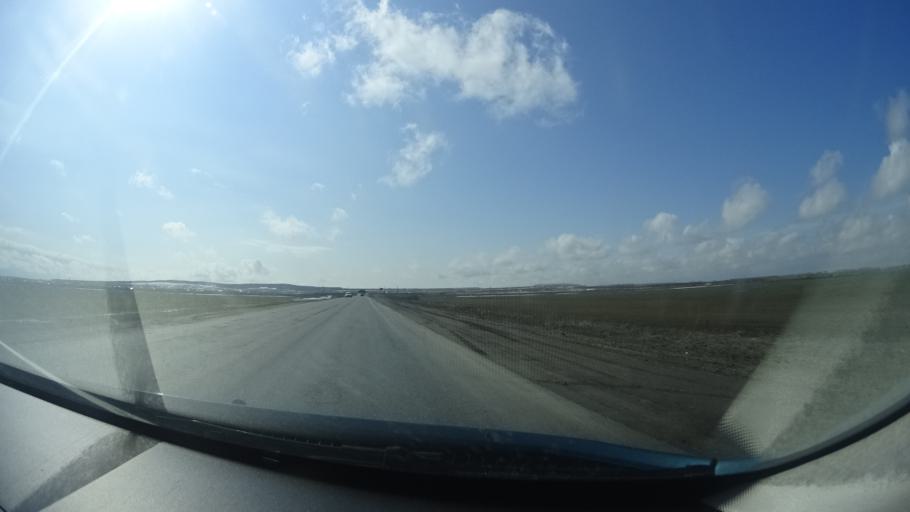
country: RU
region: Bashkortostan
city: Mikhaylovka
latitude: 54.8883
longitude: 55.7185
